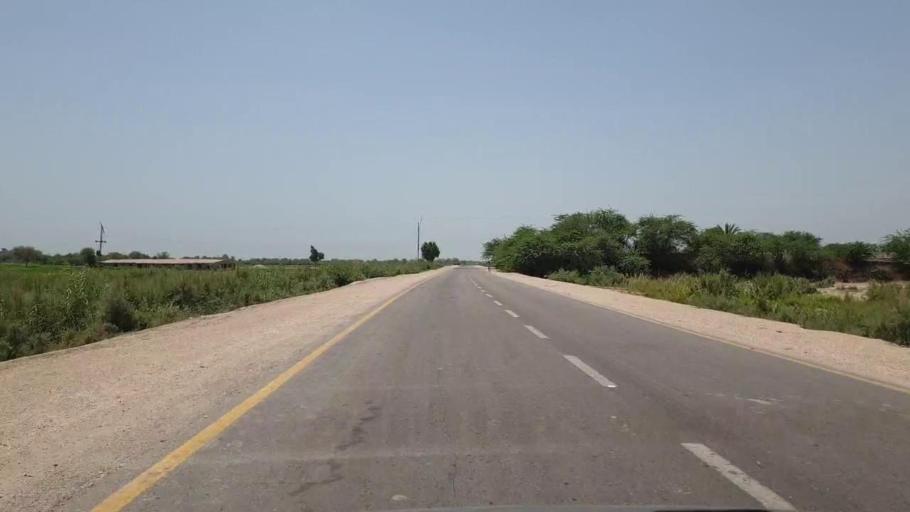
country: PK
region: Sindh
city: Sakrand
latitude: 26.1233
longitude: 68.3826
